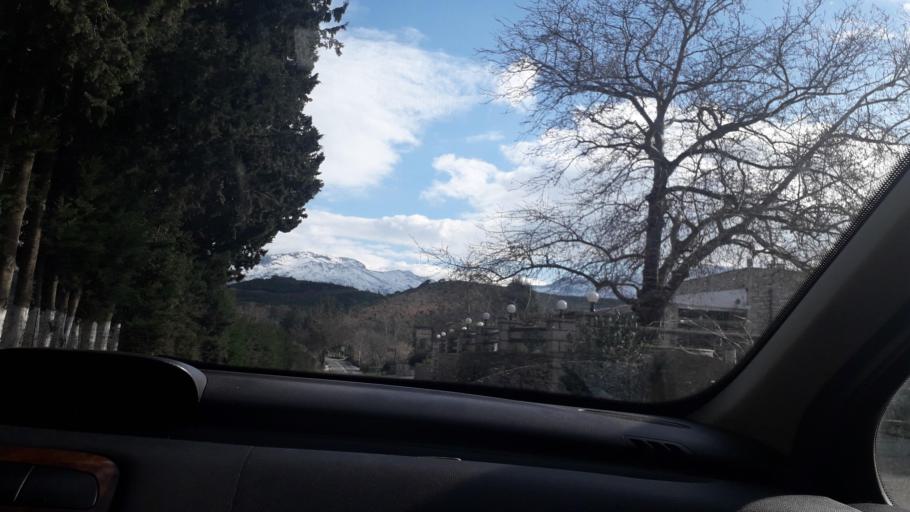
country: GR
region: Crete
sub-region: Nomos Rethymnis
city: Agia Foteini
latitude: 35.2914
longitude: 24.5601
